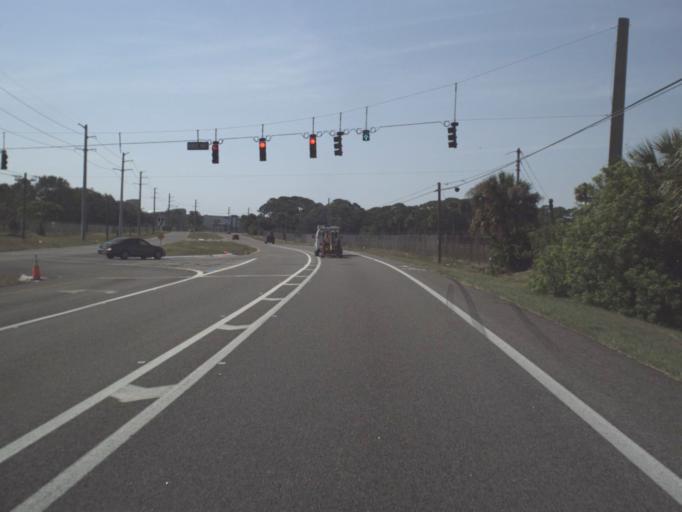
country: US
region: Florida
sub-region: Brevard County
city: Port Saint John
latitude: 28.4907
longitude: -80.7751
